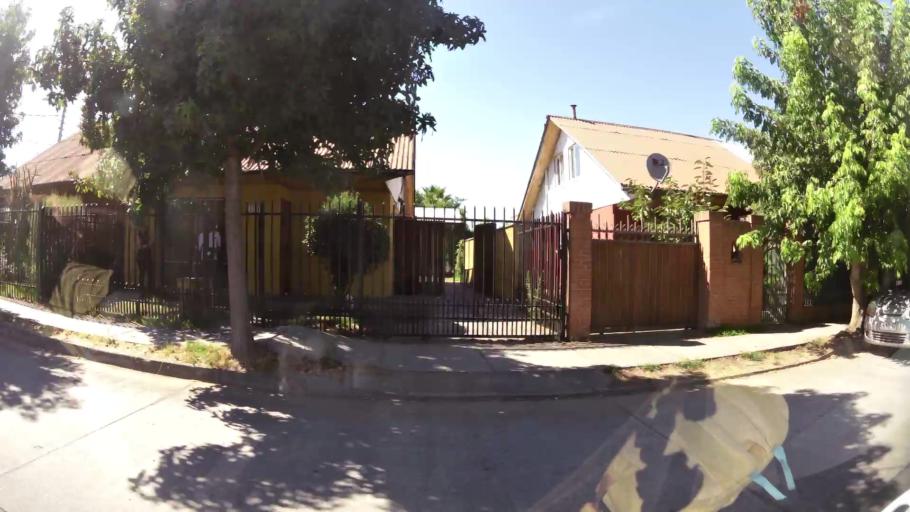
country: CL
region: Maule
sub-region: Provincia de Curico
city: Curico
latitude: -34.9724
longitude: -71.2590
